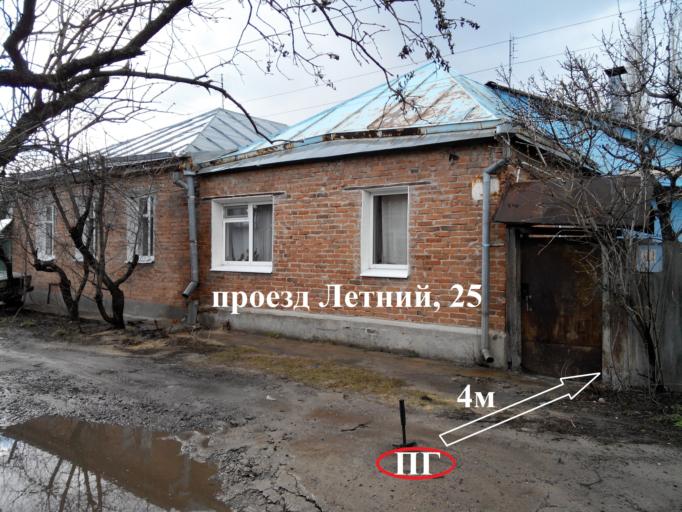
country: RU
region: Voronezj
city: Voronezh
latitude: 51.6379
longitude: 39.1613
